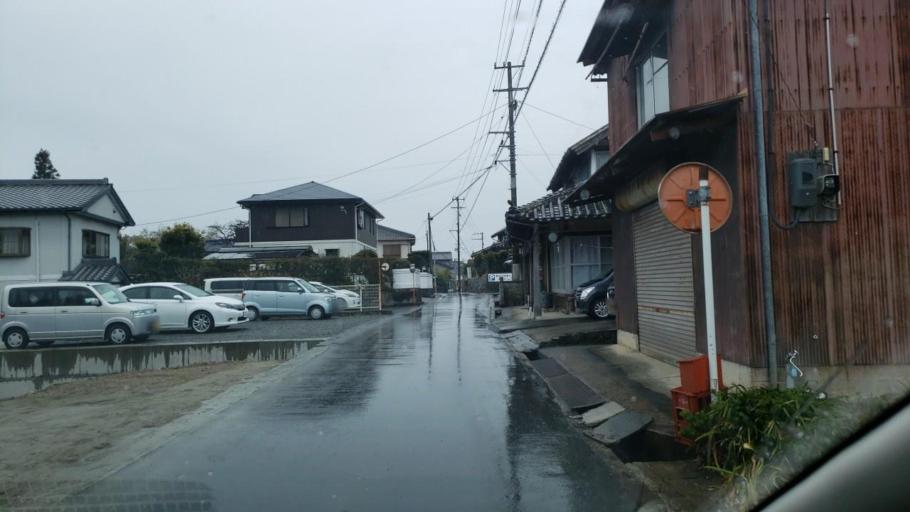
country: JP
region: Tokushima
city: Wakimachi
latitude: 34.0779
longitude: 134.2469
